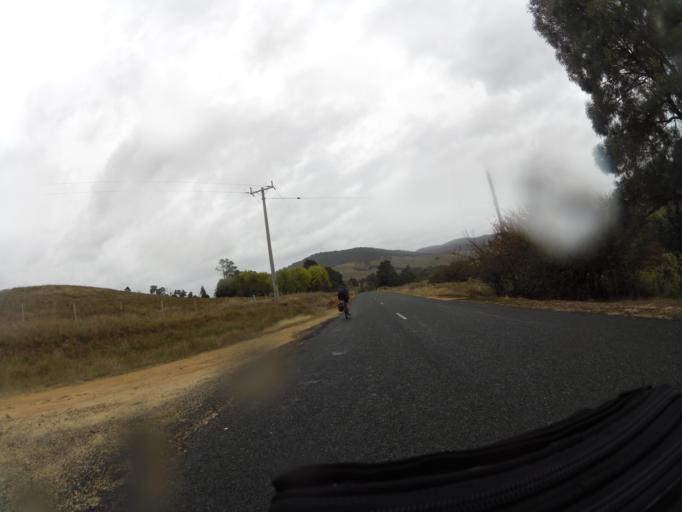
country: AU
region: New South Wales
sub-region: Greater Hume Shire
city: Holbrook
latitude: -36.2360
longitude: 147.6494
